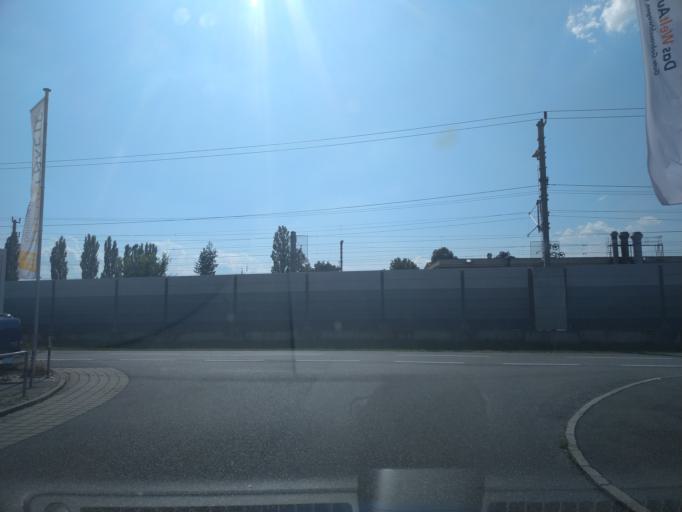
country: AT
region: Styria
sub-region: Politischer Bezirk Leibnitz
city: Leibnitz
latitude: 46.7762
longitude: 15.5491
